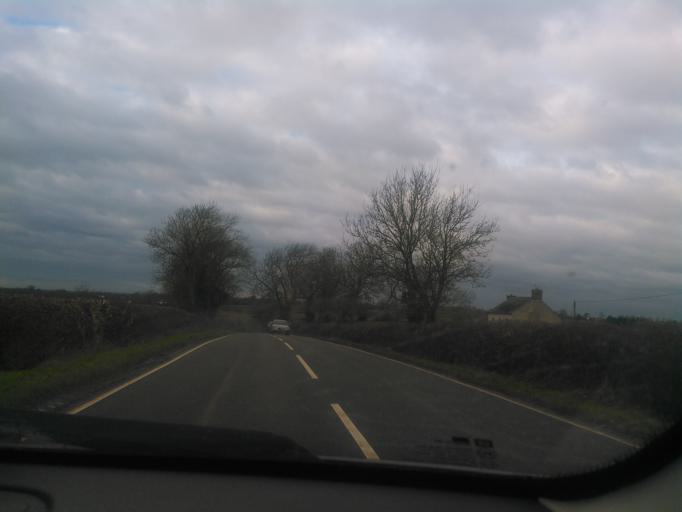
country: GB
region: England
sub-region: Leicestershire
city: Wigston Magna
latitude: 52.5749
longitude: -1.0800
